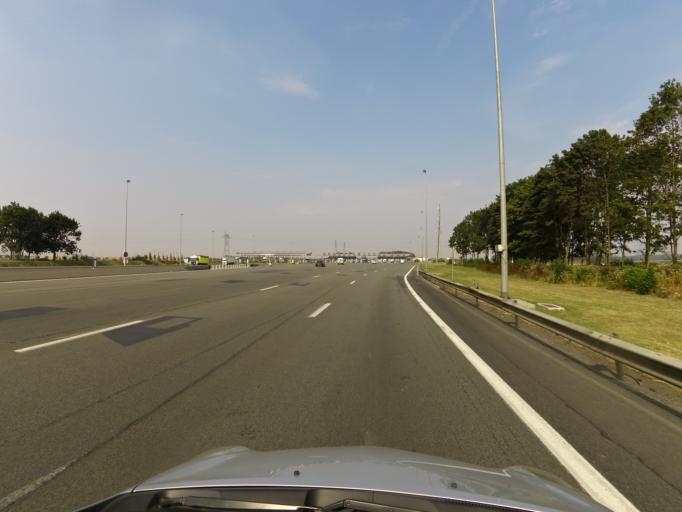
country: FR
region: Nord-Pas-de-Calais
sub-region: Departement du Pas-de-Calais
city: Roeux
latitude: 50.3230
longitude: 2.9097
